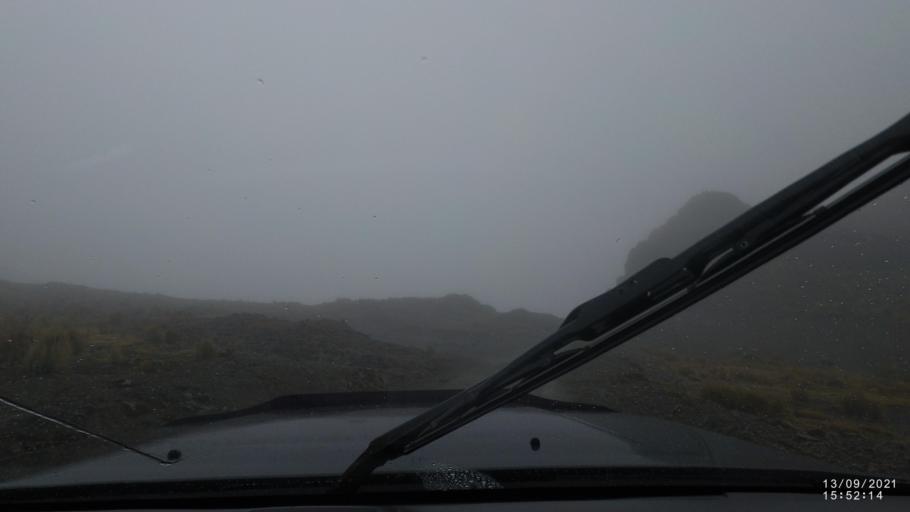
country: BO
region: Cochabamba
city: Colomi
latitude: -17.3039
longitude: -65.7127
